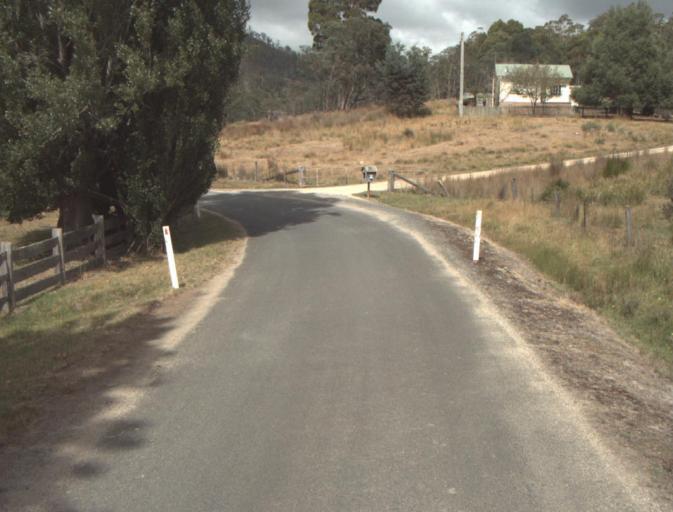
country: AU
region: Tasmania
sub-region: Northern Midlands
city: Evandale
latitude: -41.4873
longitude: 147.4385
